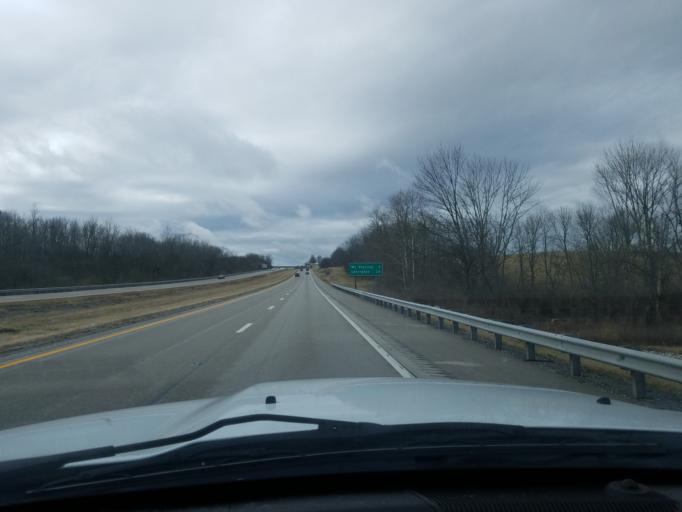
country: US
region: Kentucky
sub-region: Montgomery County
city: Mount Sterling
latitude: 38.0866
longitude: -83.9153
